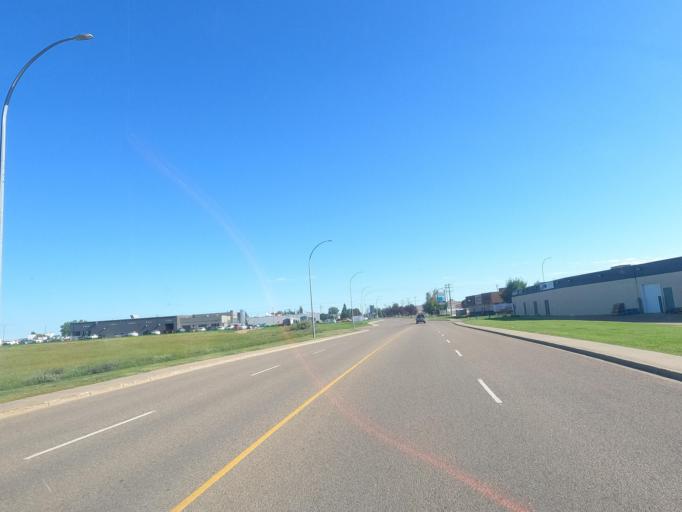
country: CA
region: Alberta
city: Brooks
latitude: 50.5744
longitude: -111.9007
